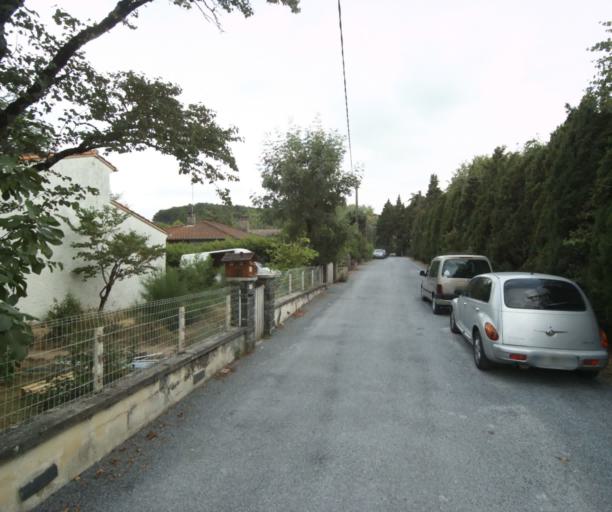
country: FR
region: Midi-Pyrenees
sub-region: Departement de la Haute-Garonne
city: Revel
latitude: 43.4420
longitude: 2.0282
